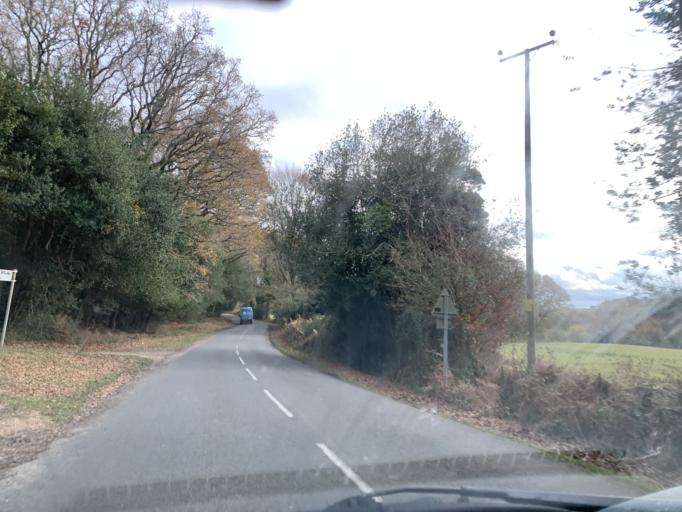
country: GB
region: England
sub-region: Hampshire
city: Lyndhurst
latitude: 50.8921
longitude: -1.6193
